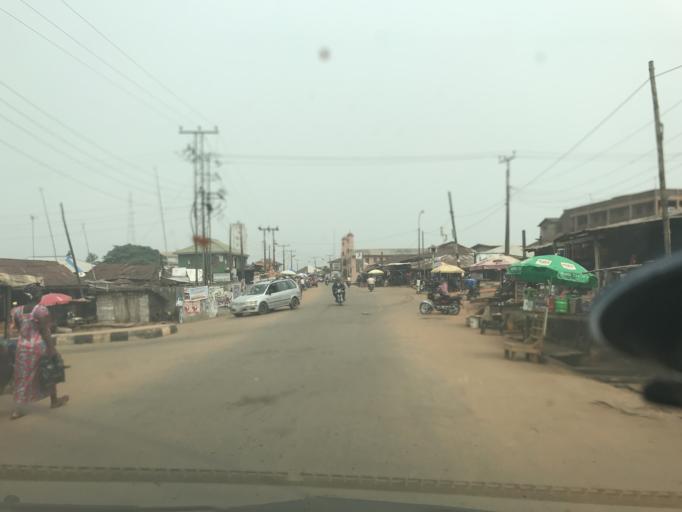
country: NG
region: Ogun
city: Ilaro
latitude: 6.8871
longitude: 3.0210
